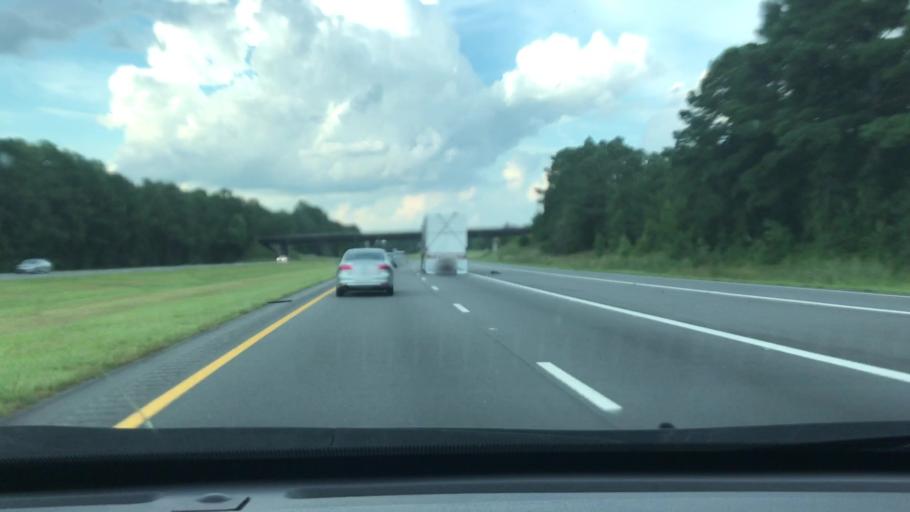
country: US
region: North Carolina
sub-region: Cumberland County
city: Vander
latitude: 35.0515
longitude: -78.8001
